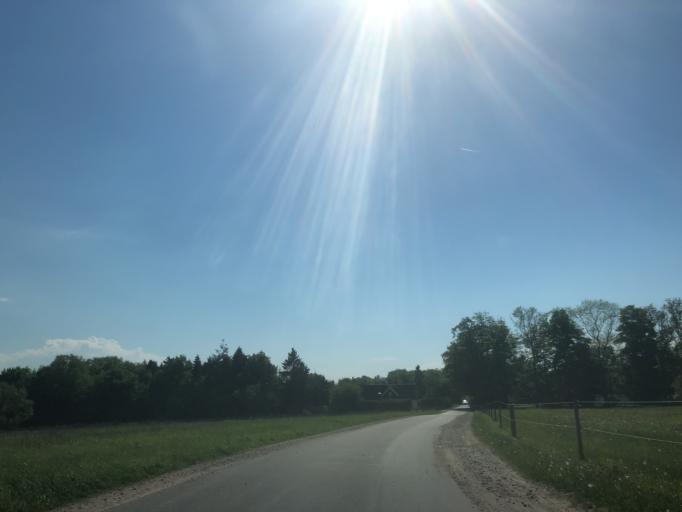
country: DK
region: Zealand
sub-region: Roskilde Kommune
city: Vindinge
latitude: 55.6180
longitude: 12.1185
